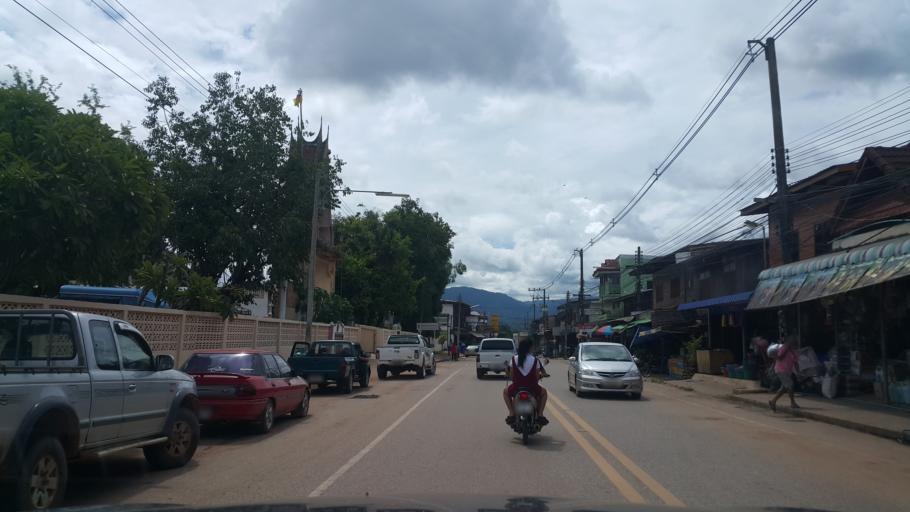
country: TH
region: Phitsanulok
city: Chat Trakan
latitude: 17.2753
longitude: 100.6023
